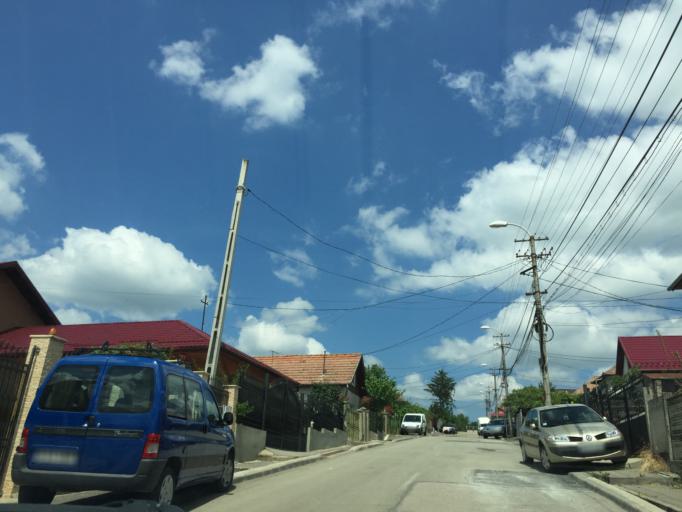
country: RO
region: Cluj
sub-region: Municipiul Cluj-Napoca
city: Cluj-Napoca
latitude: 46.7909
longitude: 23.5625
